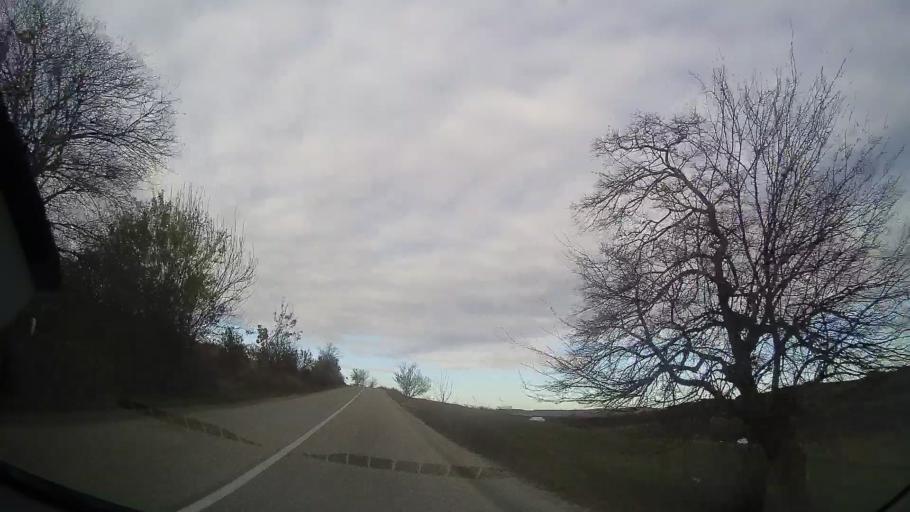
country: RO
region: Bistrita-Nasaud
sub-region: Comuna Budesti
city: Budesti
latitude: 46.8912
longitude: 24.2508
